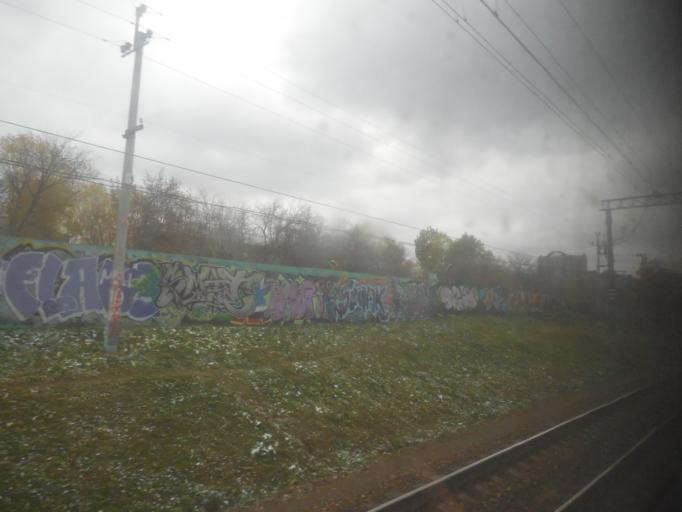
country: RU
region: Moscow
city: Davydkovo
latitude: 55.7278
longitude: 37.4570
